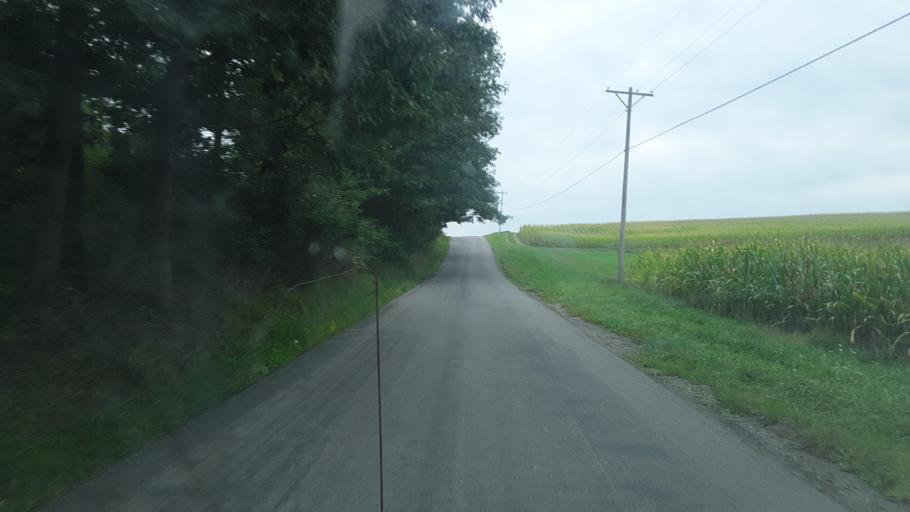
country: US
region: Pennsylvania
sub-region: Jefferson County
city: Punxsutawney
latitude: 40.9469
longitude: -79.1374
